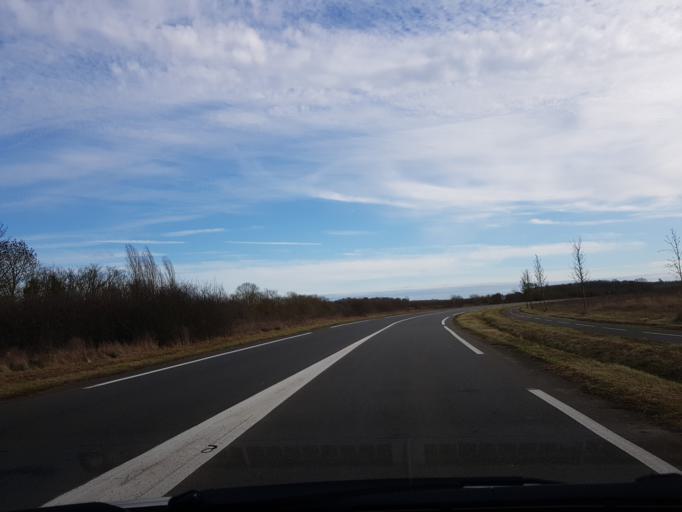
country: FR
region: Centre
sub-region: Departement du Loiret
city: Saint-Denis-en-Val
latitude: 47.8762
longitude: 1.9854
